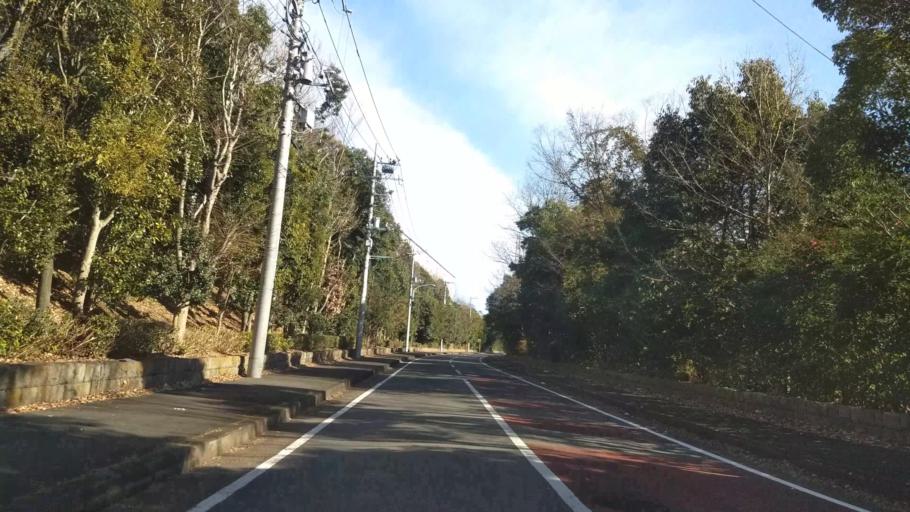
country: JP
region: Kanagawa
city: Hadano
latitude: 35.3447
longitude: 139.2222
